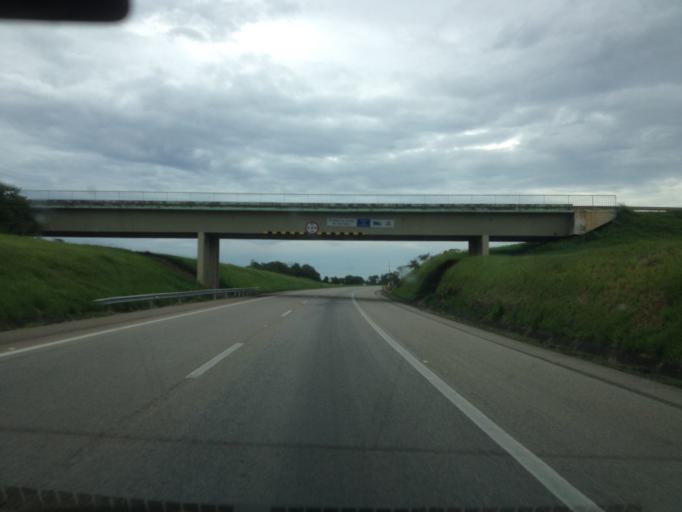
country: BR
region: Sao Paulo
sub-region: Boituva
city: Boituva
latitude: -23.3172
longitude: -47.6367
